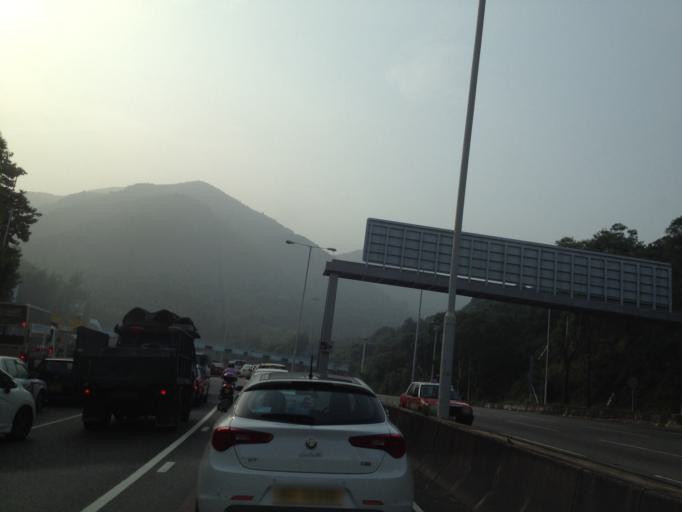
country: HK
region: Sha Tin
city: Sha Tin
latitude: 22.3787
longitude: 114.2107
